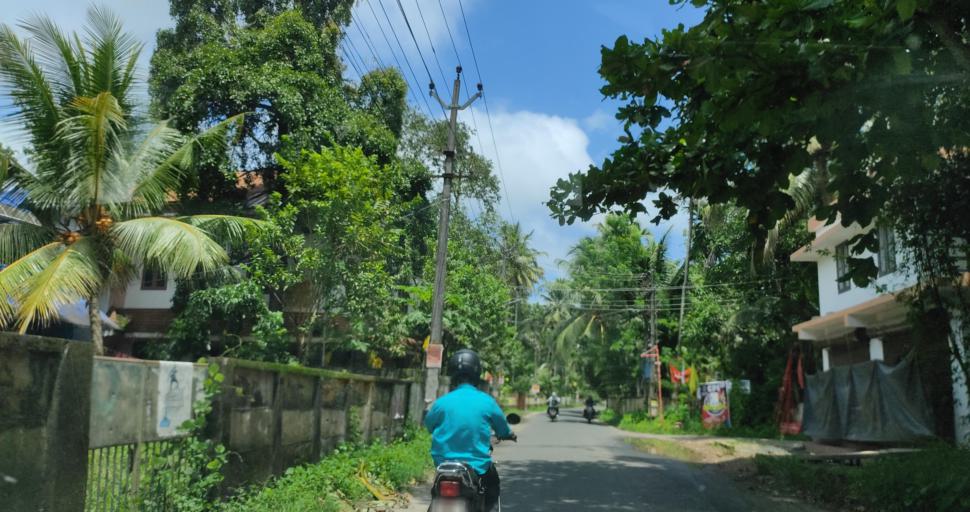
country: IN
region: Kerala
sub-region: Alappuzha
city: Vayalar
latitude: 9.7056
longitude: 76.3389
